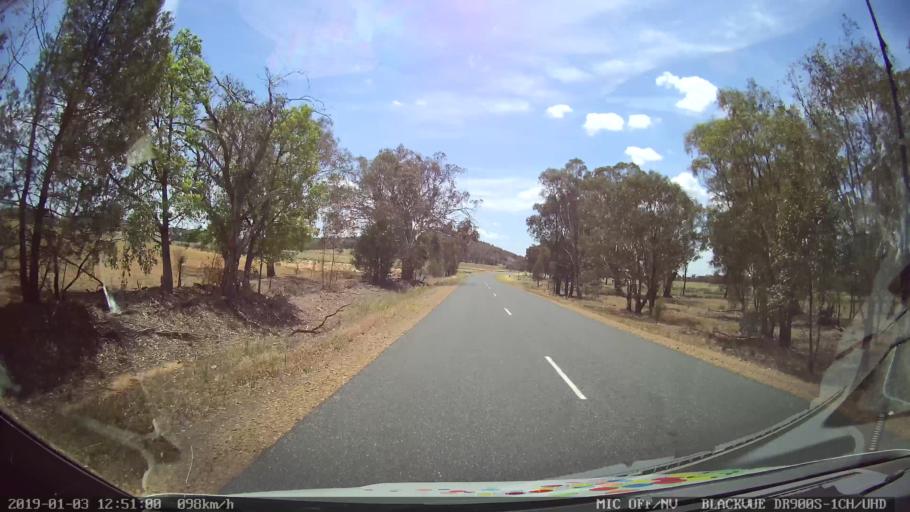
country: AU
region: New South Wales
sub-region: Weddin
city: Grenfell
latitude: -33.6846
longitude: 148.2757
